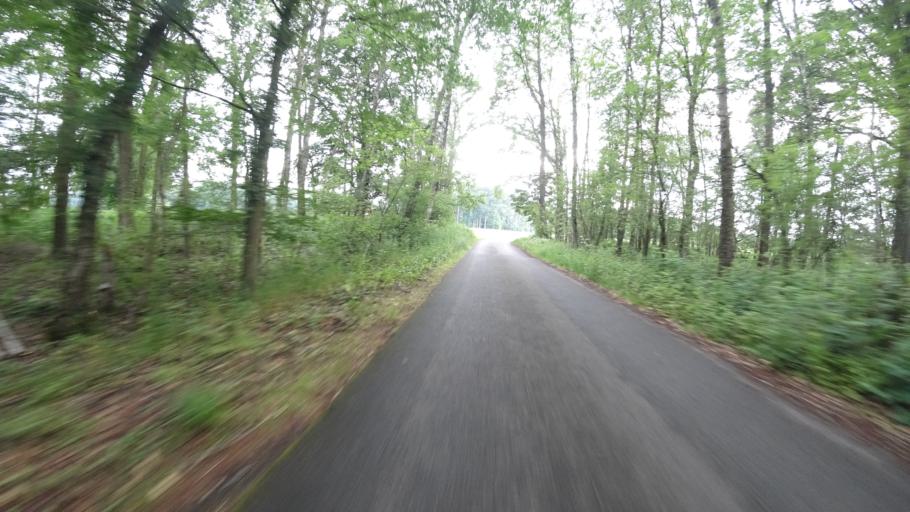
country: DE
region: North Rhine-Westphalia
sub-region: Regierungsbezirk Detmold
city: Guetersloh
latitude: 51.9479
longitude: 8.3325
